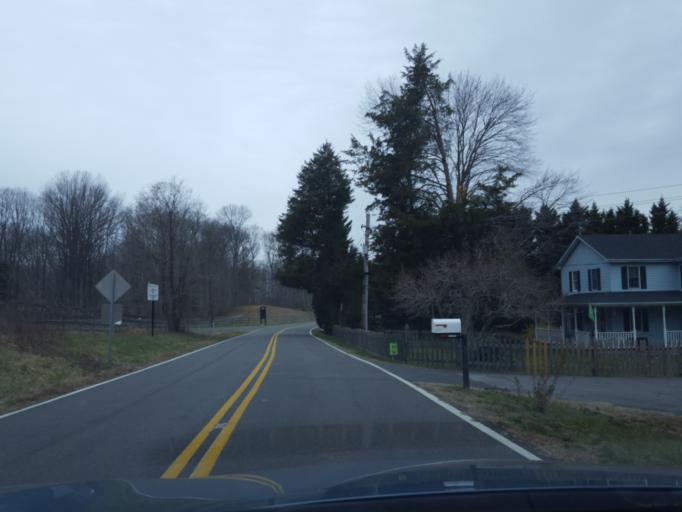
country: US
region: Maryland
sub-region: Calvert County
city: Prince Frederick
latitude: 38.4855
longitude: -76.5818
